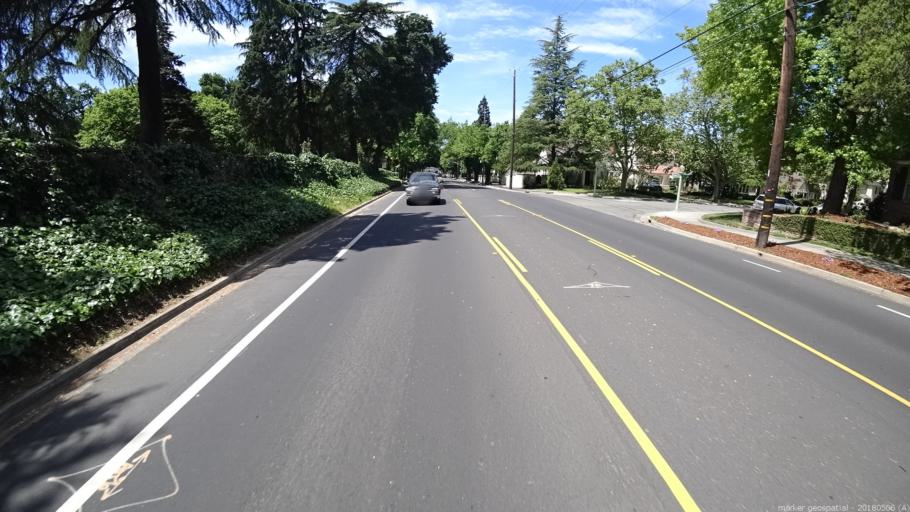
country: US
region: California
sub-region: Sacramento County
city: Sacramento
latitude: 38.5632
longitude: -121.4505
